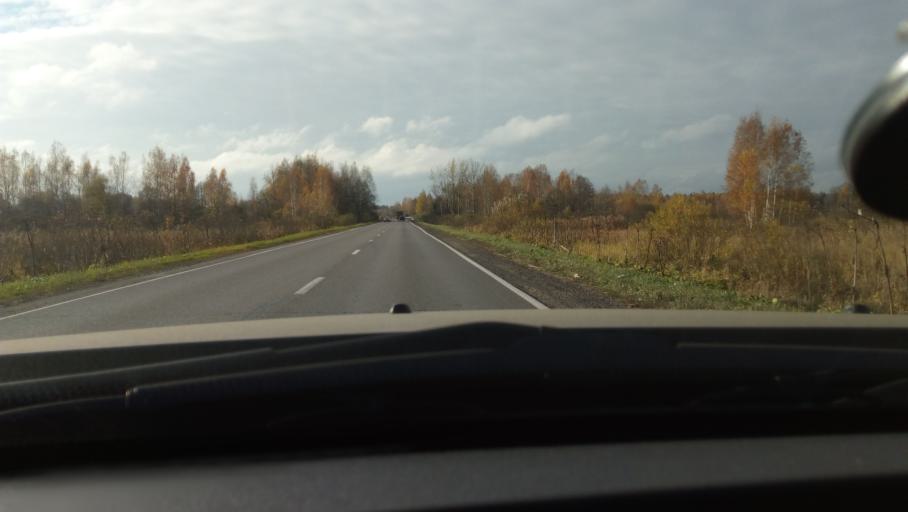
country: RU
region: Moskovskaya
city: Fryazevo
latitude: 55.7347
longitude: 38.5054
